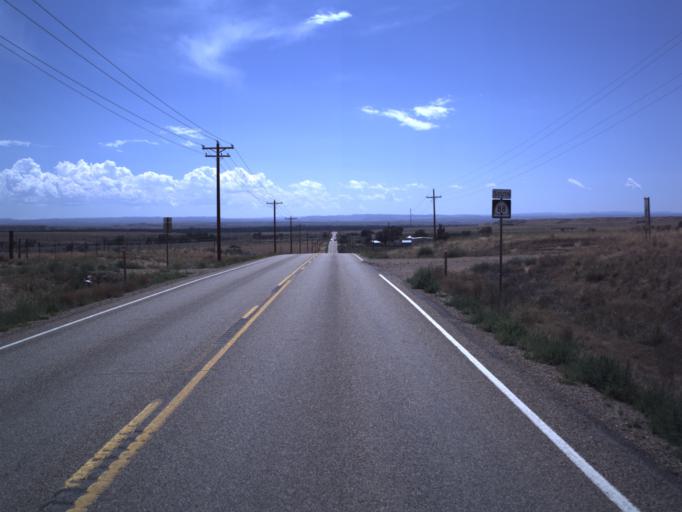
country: US
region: Utah
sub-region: Uintah County
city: Naples
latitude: 40.1558
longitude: -109.6642
